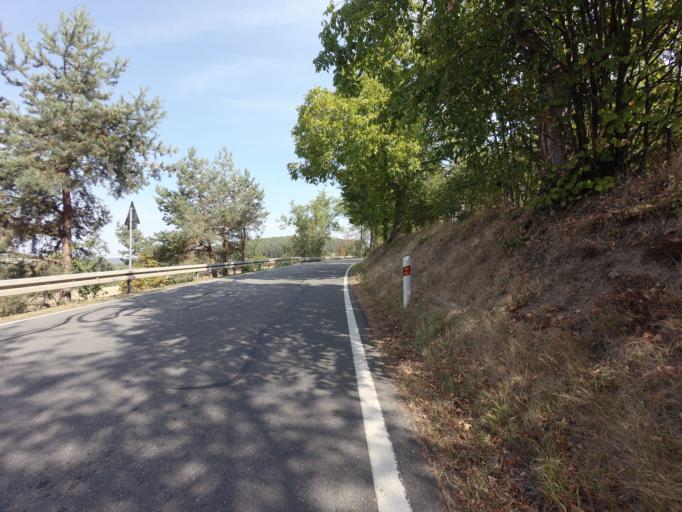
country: CZ
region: Central Bohemia
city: Petrovice
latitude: 49.5768
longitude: 14.3759
